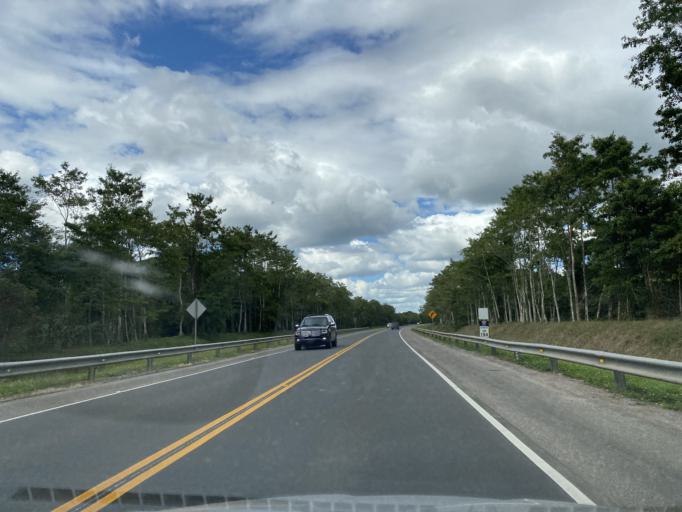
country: DO
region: Santo Domingo
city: Guerra
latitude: 18.5936
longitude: -69.7707
